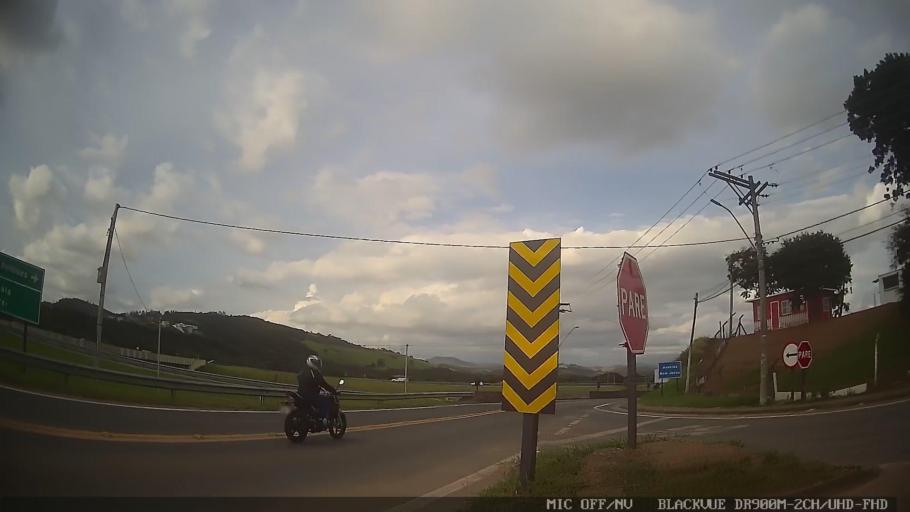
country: BR
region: Sao Paulo
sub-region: Bom Jesus Dos Perdoes
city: Bom Jesus dos Perdoes
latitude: -23.1159
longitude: -46.4813
